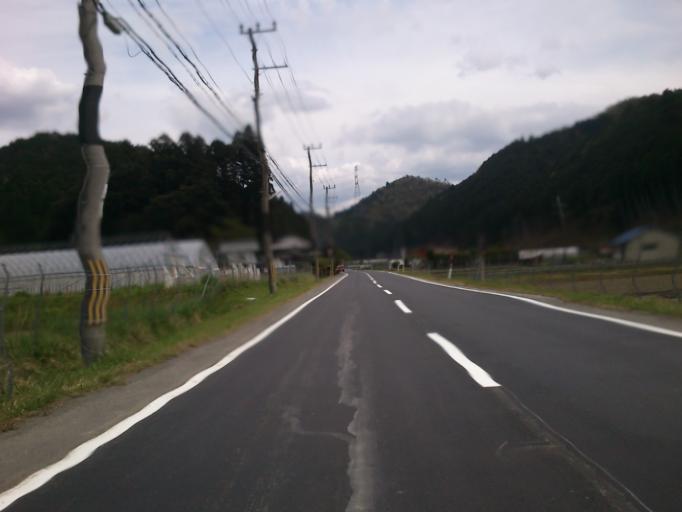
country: JP
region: Kyoto
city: Kameoka
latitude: 35.2062
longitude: 135.6060
